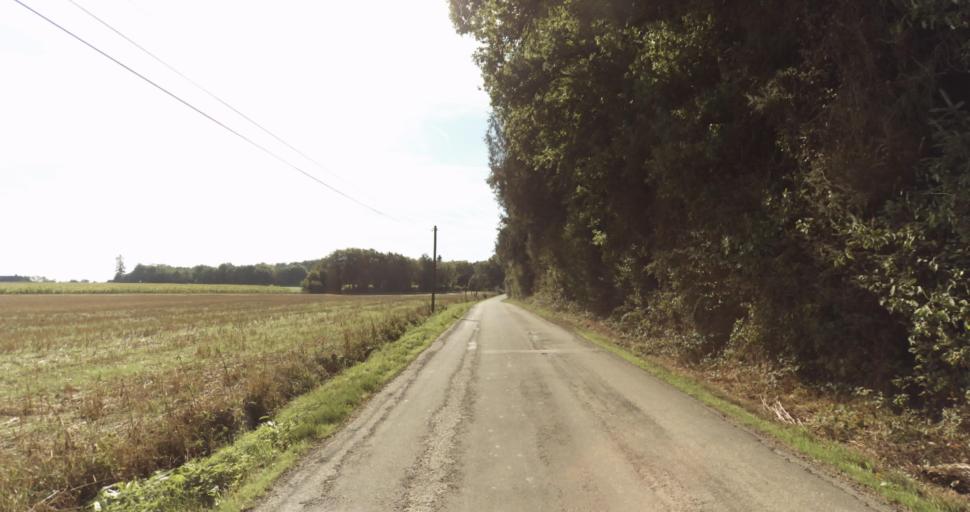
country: FR
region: Lower Normandy
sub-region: Departement du Calvados
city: La Vespiere
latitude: 48.9247
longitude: 0.3421
